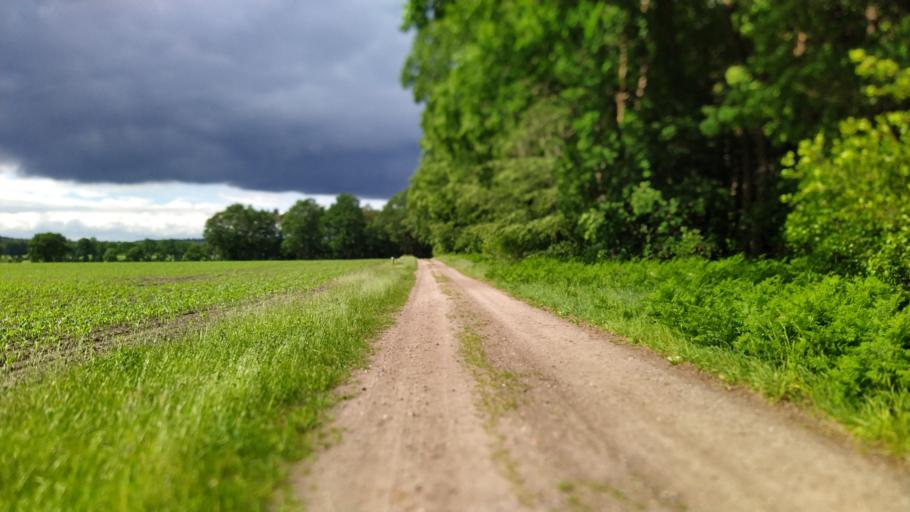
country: DE
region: Lower Saxony
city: Deinstedt
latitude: 53.4383
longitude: 9.2602
